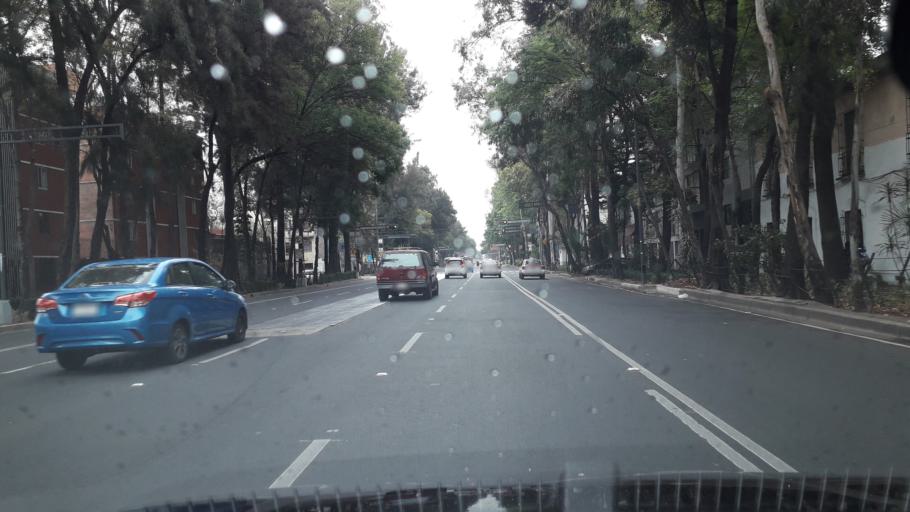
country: MX
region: Mexico City
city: Cuauhtemoc
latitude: 19.4476
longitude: -99.1611
